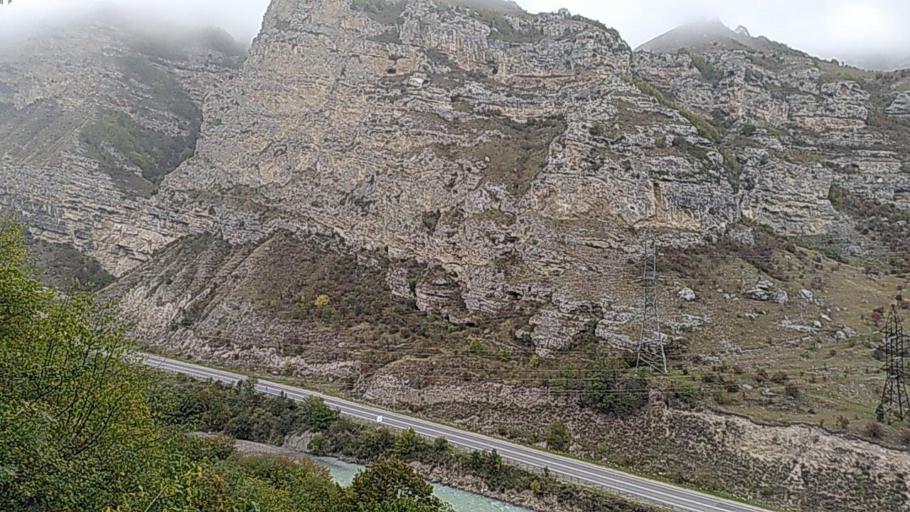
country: RU
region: Kabardino-Balkariya
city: Zhankhoteko
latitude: 43.5067
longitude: 43.1435
